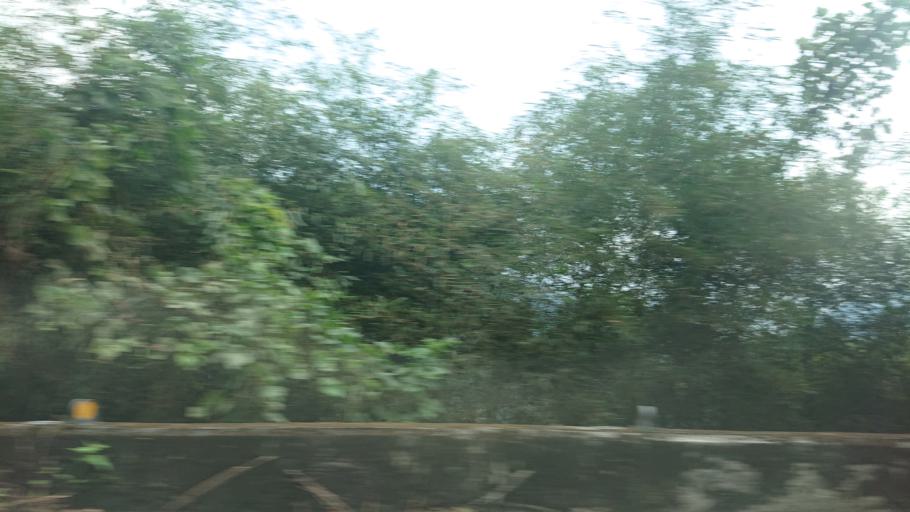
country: TW
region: Taiwan
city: Lugu
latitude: 23.5881
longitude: 120.6980
